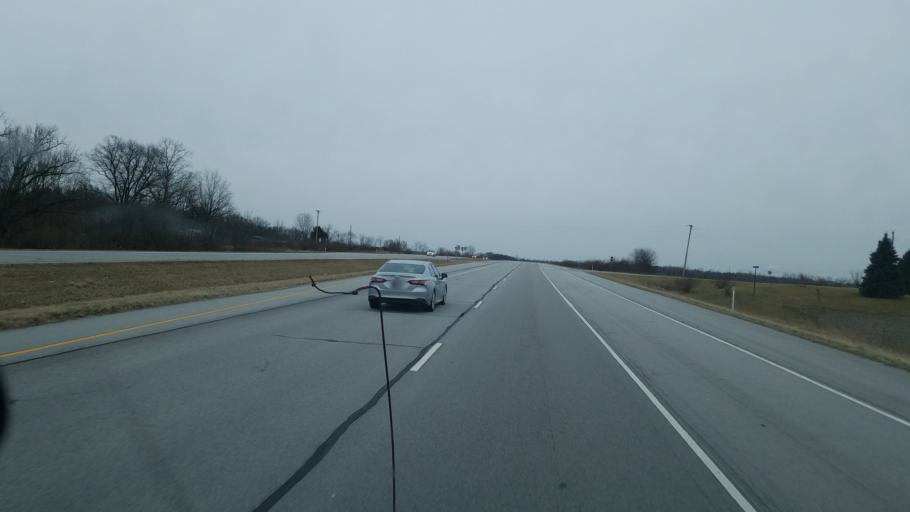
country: US
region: Indiana
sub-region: Marshall County
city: Argos
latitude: 41.2677
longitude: -86.2679
